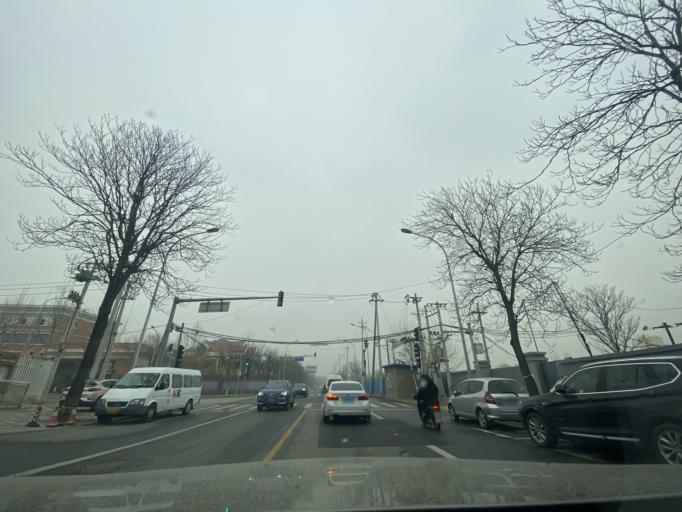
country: CN
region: Beijing
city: Sijiqing
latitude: 39.9579
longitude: 116.2416
